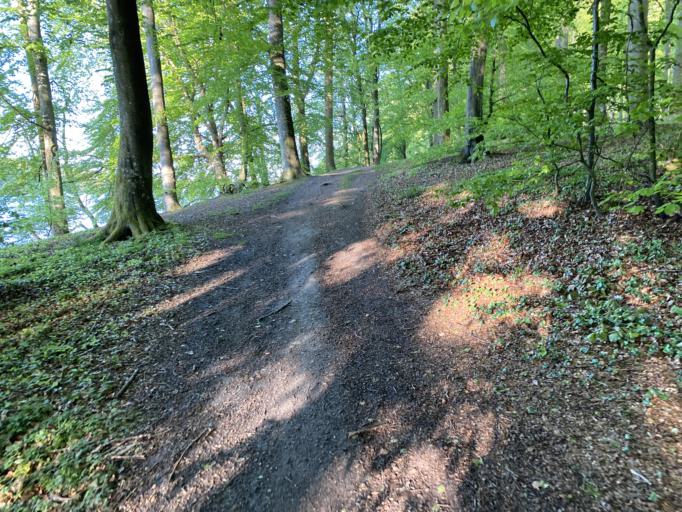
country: DK
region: Capital Region
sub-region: Fureso Kommune
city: Farum
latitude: 55.8000
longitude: 12.3416
